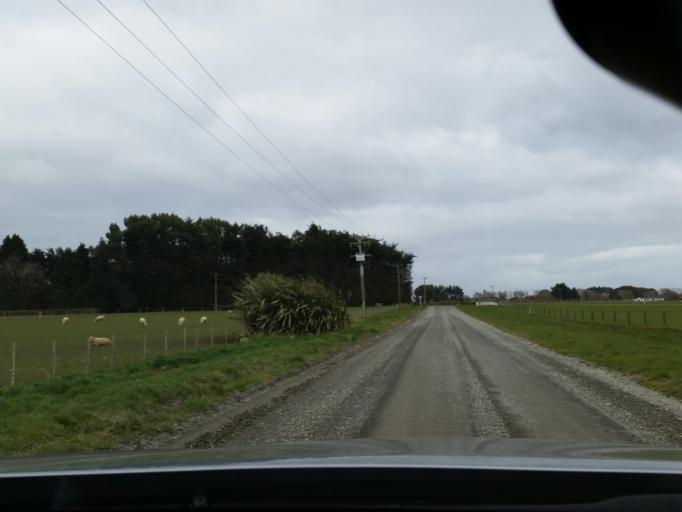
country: NZ
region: Southland
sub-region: Invercargill City
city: Invercargill
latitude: -46.3077
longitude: 168.3034
